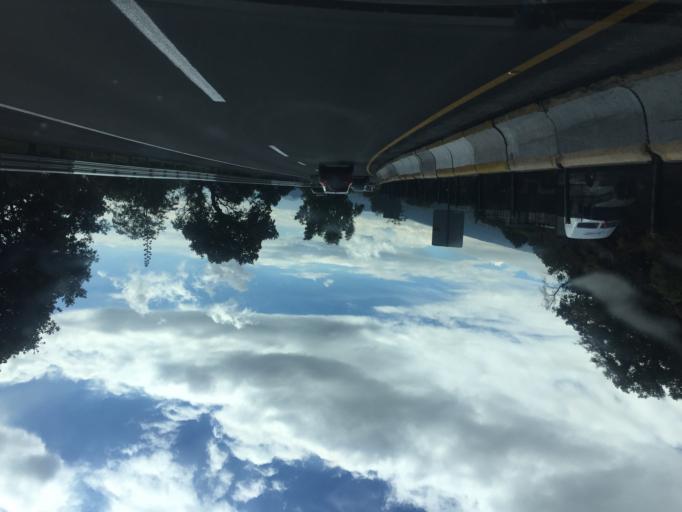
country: MX
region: Morelos
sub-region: Cuernavaca
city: Villa Santiago
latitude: 19.0243
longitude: -99.1951
